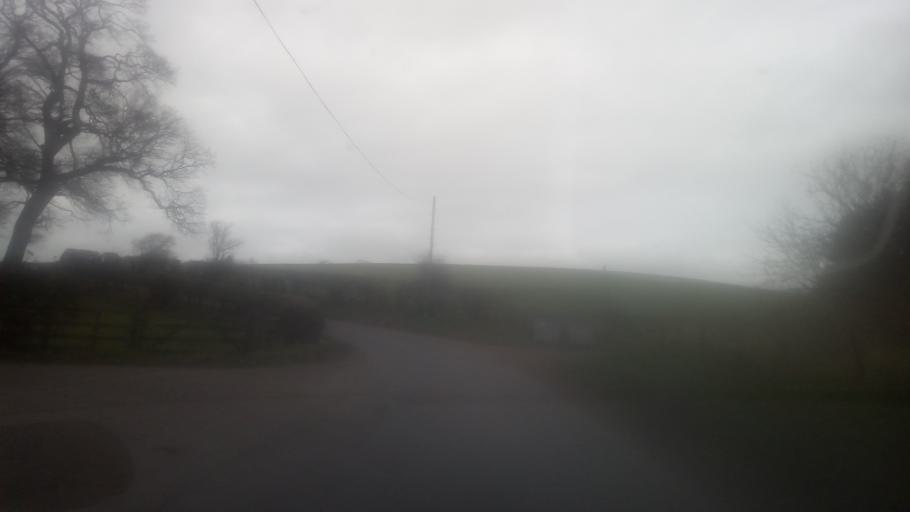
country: GB
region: Scotland
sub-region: The Scottish Borders
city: Jedburgh
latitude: 55.4924
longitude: -2.4783
